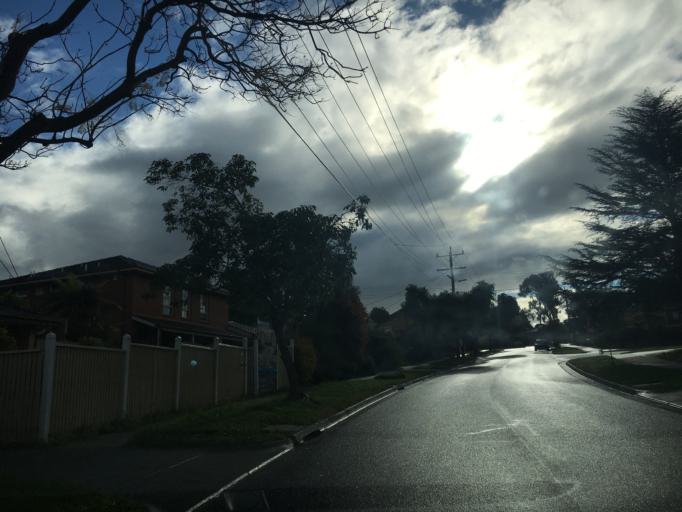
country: AU
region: Victoria
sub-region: Whitehorse
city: Vermont South
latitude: -37.8820
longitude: 145.1835
